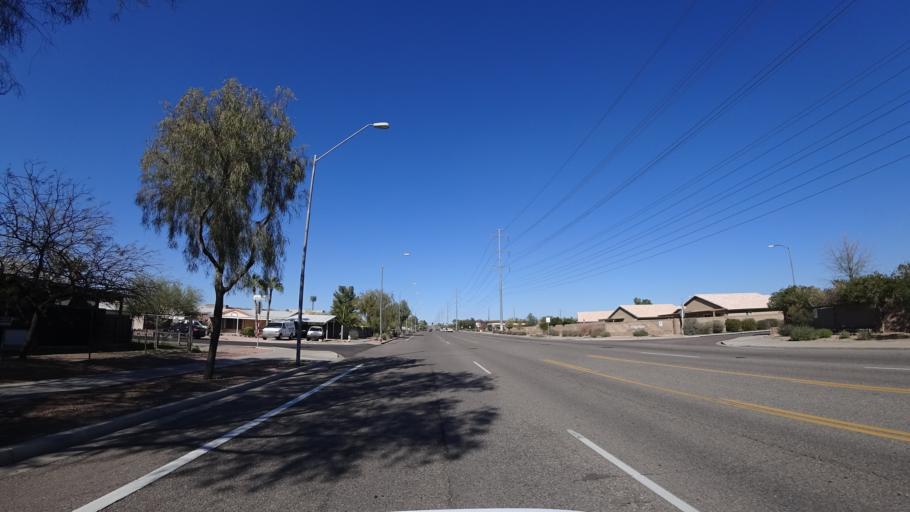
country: US
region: Arizona
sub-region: Maricopa County
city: Peoria
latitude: 33.6812
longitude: -112.1348
